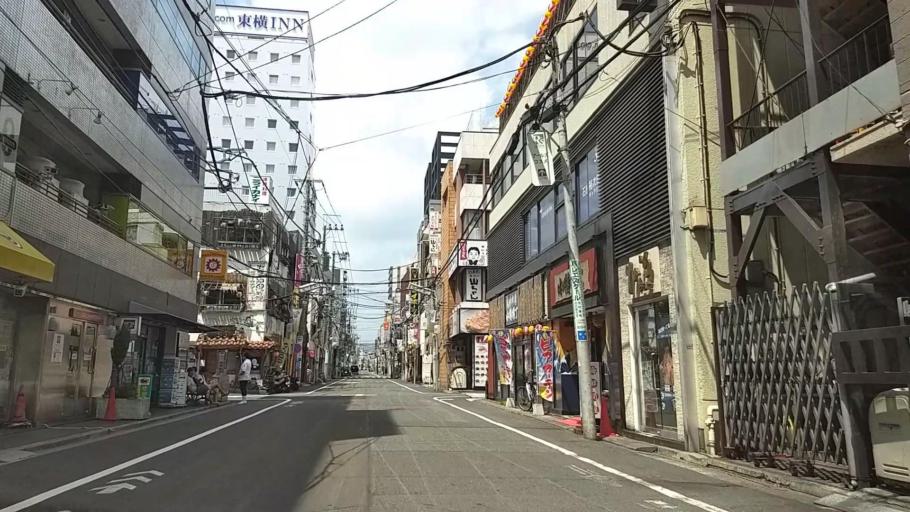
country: JP
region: Tokyo
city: Hachioji
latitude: 35.6569
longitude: 139.3379
